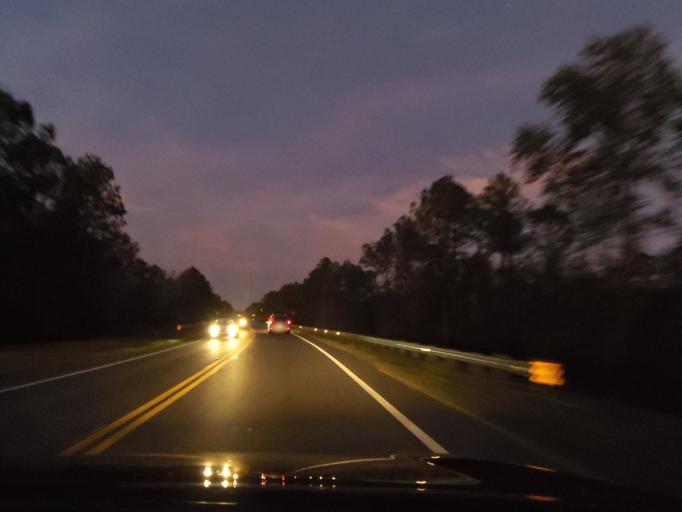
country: US
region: Florida
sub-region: Volusia County
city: De Leon Springs
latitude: 29.2403
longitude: -81.2311
